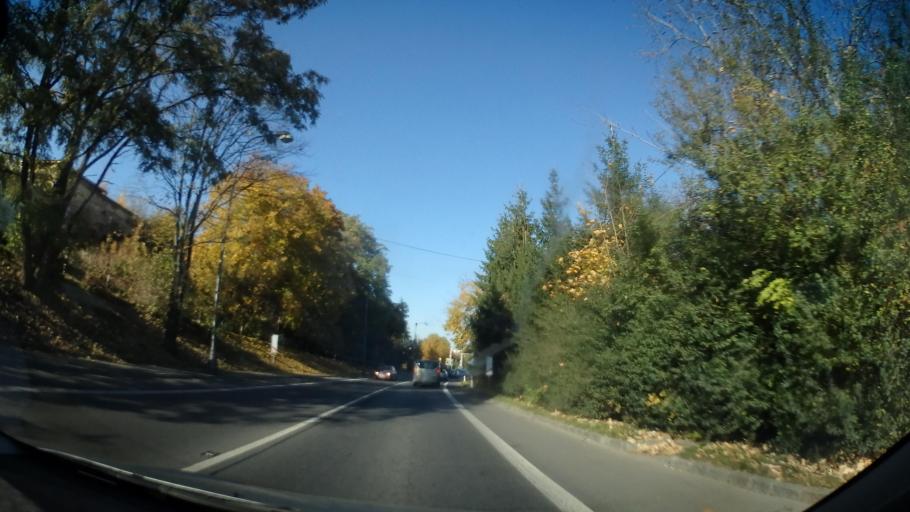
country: CZ
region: Pardubicky
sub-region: Okres Chrudim
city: Chrudim
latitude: 49.9390
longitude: 15.7947
